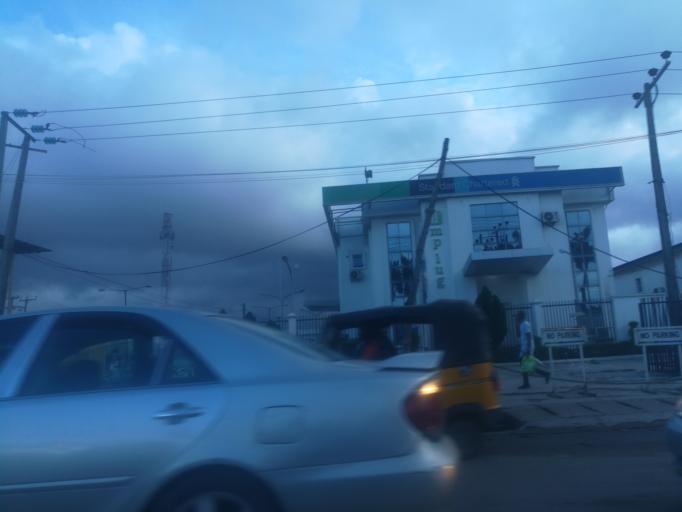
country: NG
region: Lagos
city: Agege
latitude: 6.6276
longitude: 3.3542
